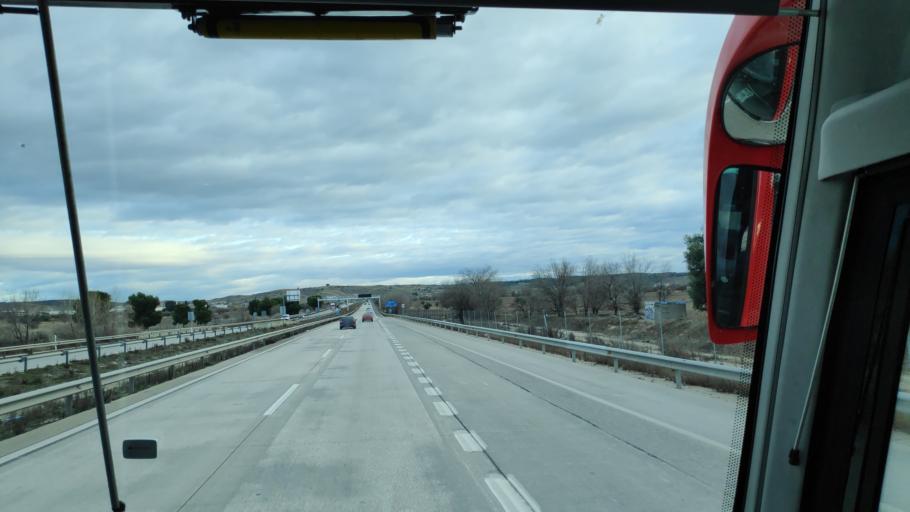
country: ES
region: Madrid
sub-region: Provincia de Madrid
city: Vaciamadrid
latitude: 40.3079
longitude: -3.4907
